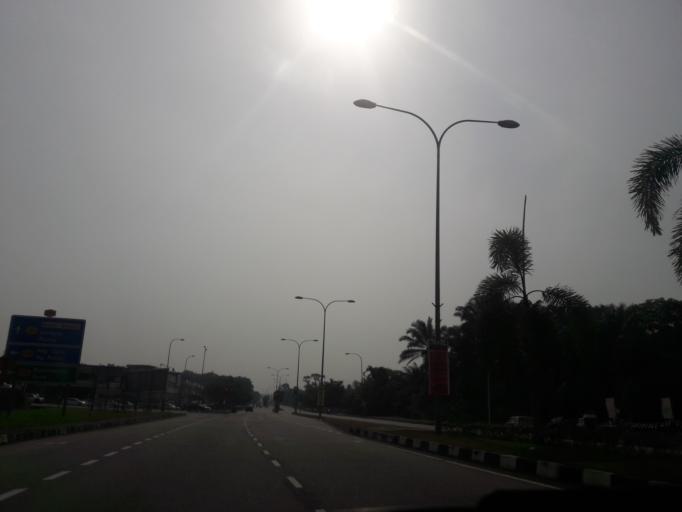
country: MY
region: Kedah
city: Kulim
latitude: 5.3523
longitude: 100.5305
